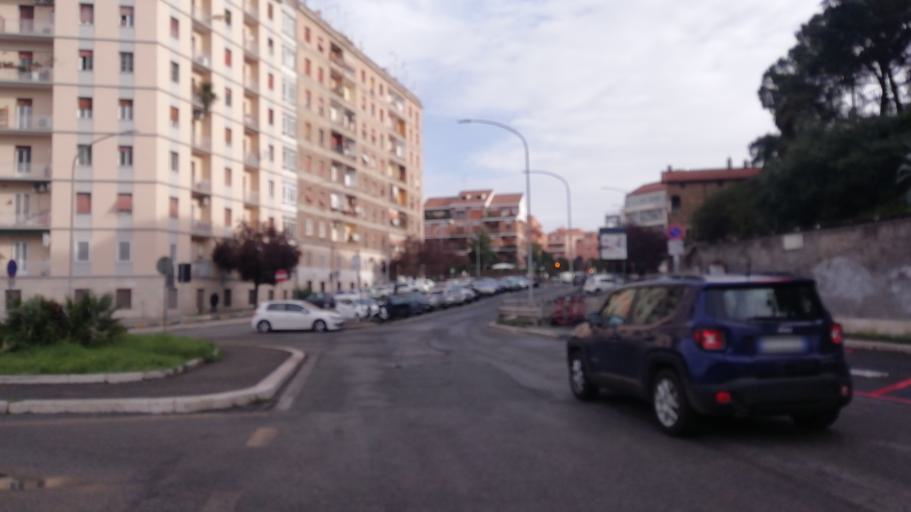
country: IT
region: Latium
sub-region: Citta metropolitana di Roma Capitale
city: Rome
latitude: 41.8737
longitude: 12.4851
